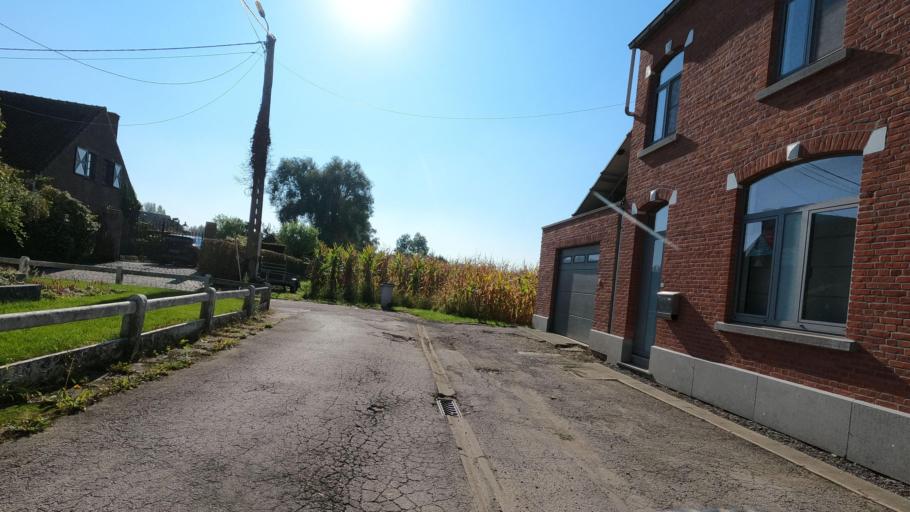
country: BE
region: Flanders
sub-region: Provincie Vlaams-Brabant
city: Holsbeek
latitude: 50.9447
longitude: 4.7436
